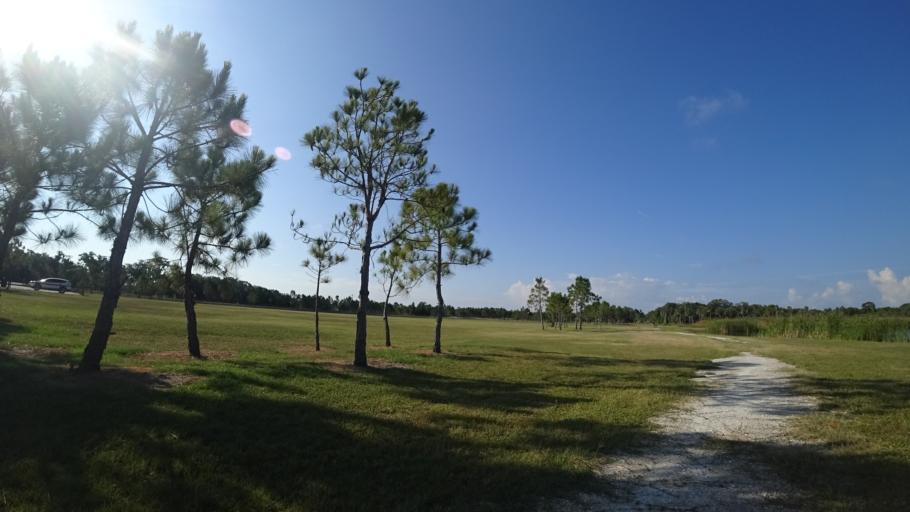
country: US
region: Florida
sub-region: Manatee County
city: Ellenton
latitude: 27.5003
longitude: -82.4877
